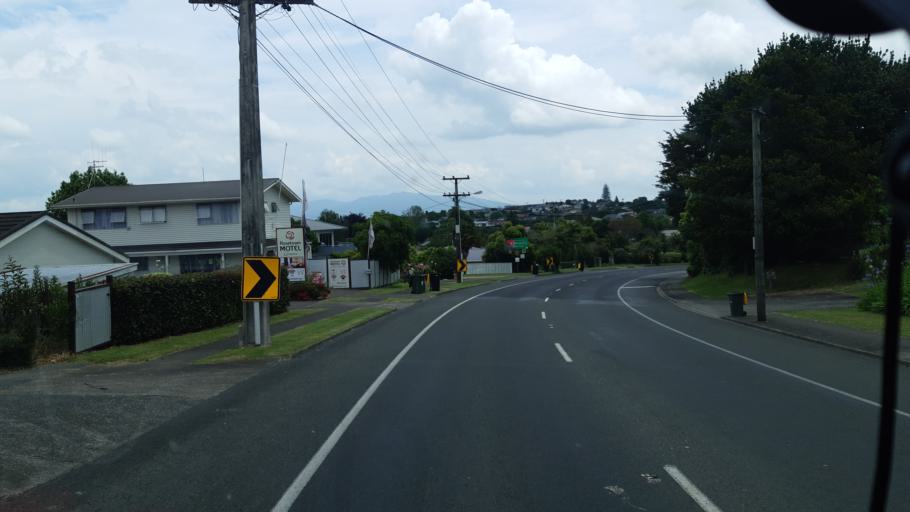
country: NZ
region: Waikato
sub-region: Waipa District
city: Cambridge
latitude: -38.0220
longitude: 175.3277
